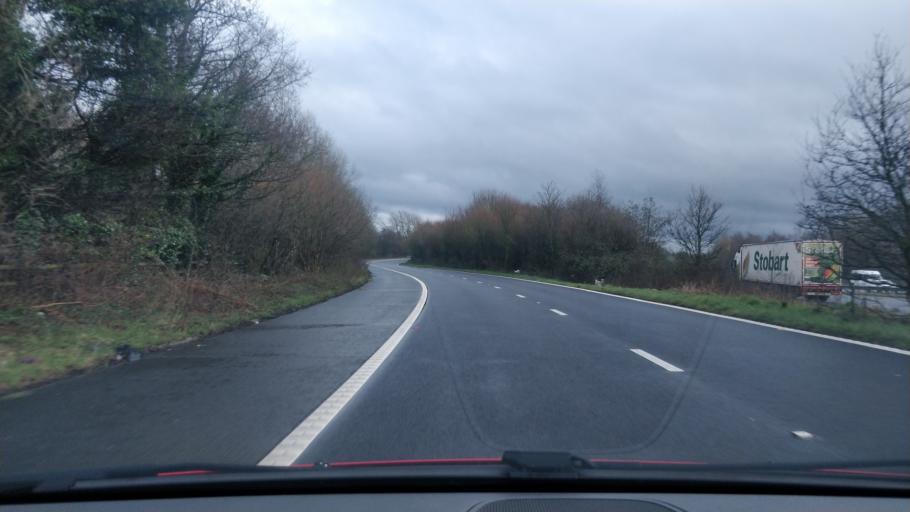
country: GB
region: England
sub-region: Knowsley
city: Knowsley
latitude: 53.4380
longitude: -2.8558
